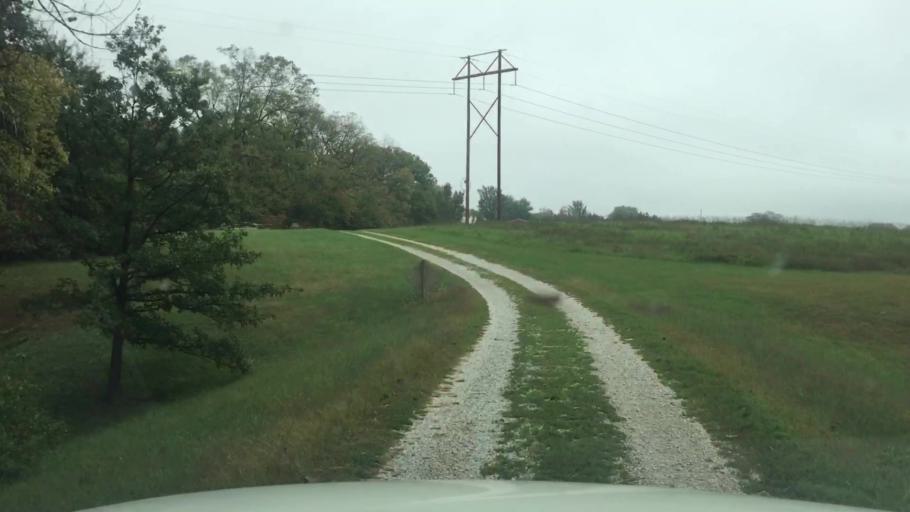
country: US
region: Missouri
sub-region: Boone County
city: Ashland
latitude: 38.8147
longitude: -92.2963
